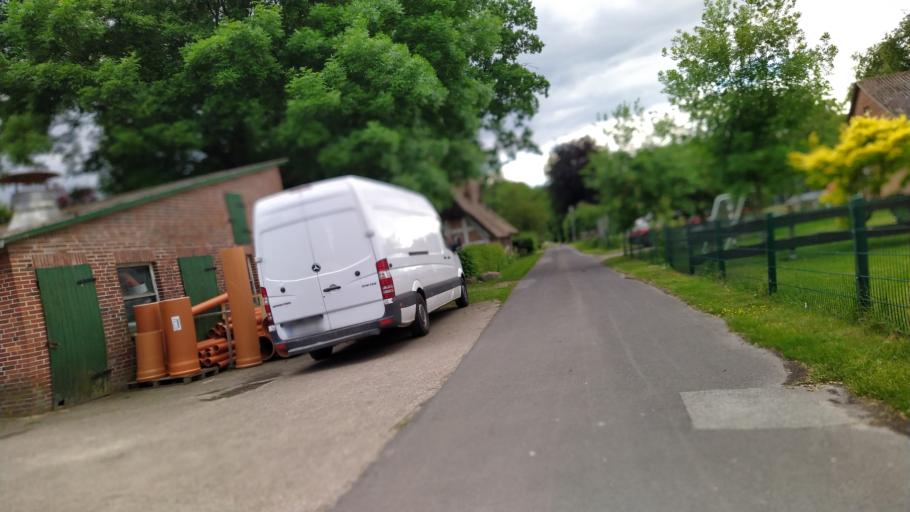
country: DE
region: Lower Saxony
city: Brest
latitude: 53.4629
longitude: 9.3731
